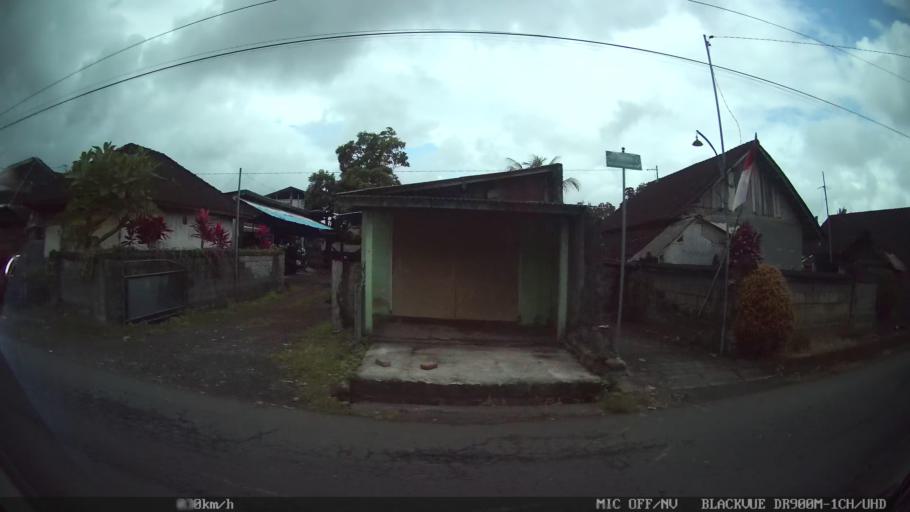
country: ID
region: Bali
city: Banjar Cemenggon
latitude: -8.5554
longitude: 115.1906
